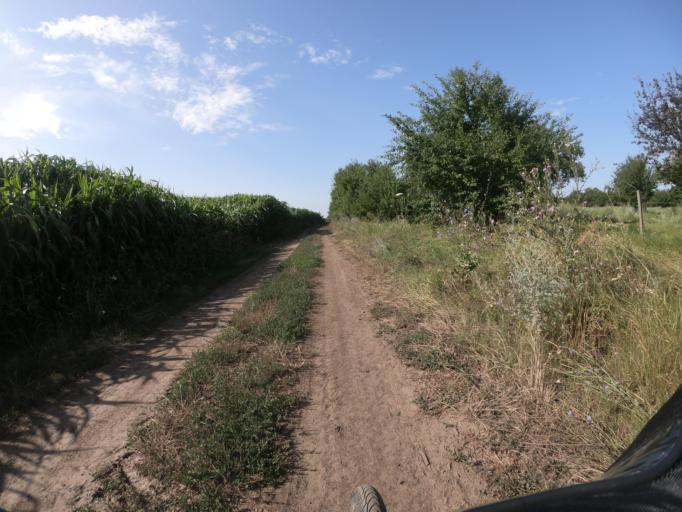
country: HU
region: Hajdu-Bihar
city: Egyek
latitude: 47.6066
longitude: 20.9810
